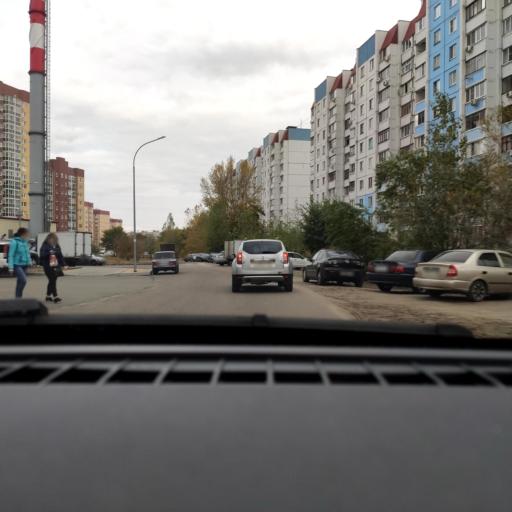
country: RU
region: Voronezj
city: Voronezh
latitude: 51.7156
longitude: 39.2690
